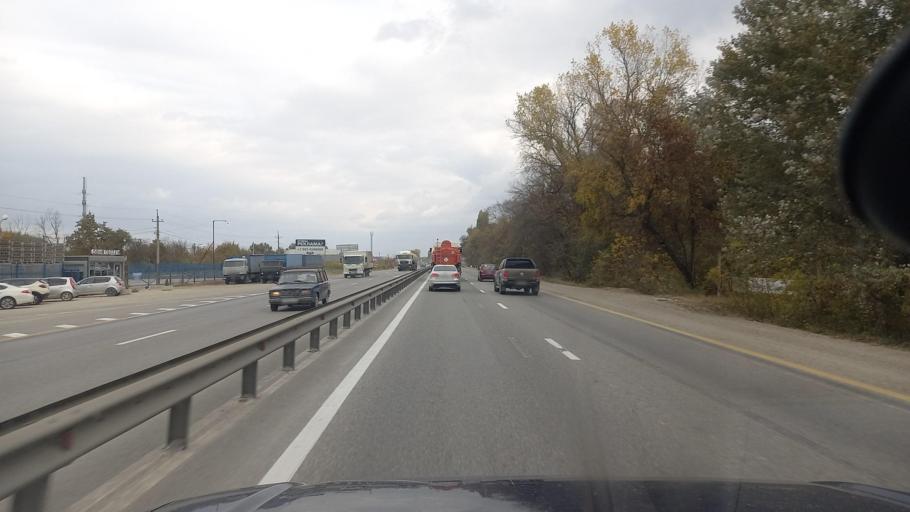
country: RU
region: Krasnodarskiy
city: Afipskiy
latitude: 44.9053
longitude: 38.8765
